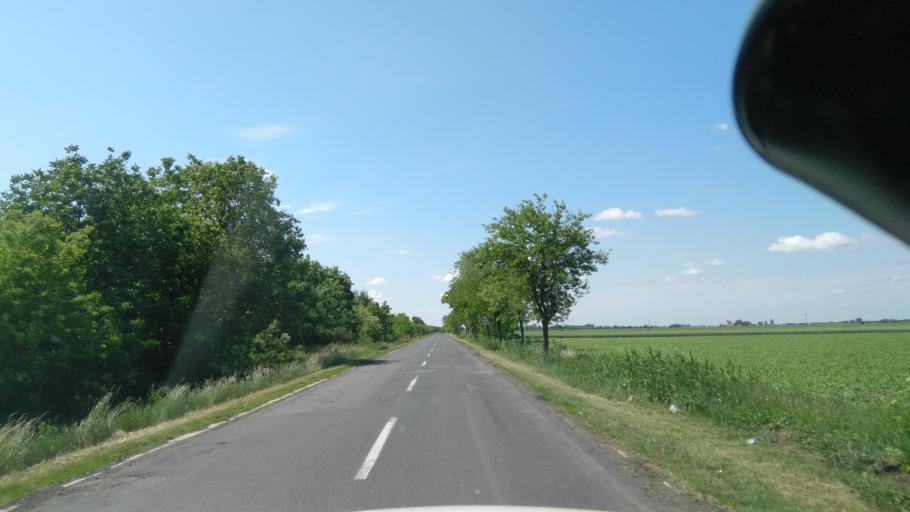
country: HU
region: Bekes
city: Medgyesegyhaza
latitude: 46.4810
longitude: 21.0221
